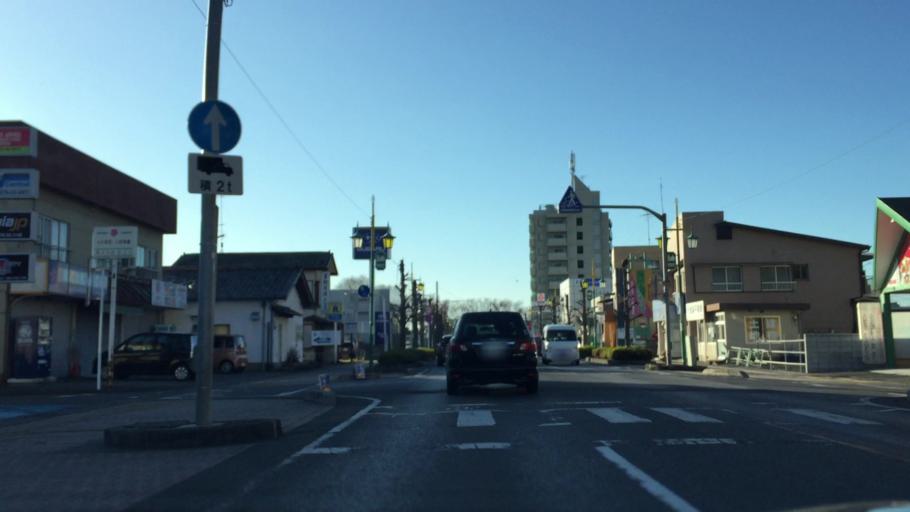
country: JP
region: Saitama
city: Menuma
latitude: 36.2598
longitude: 139.4072
